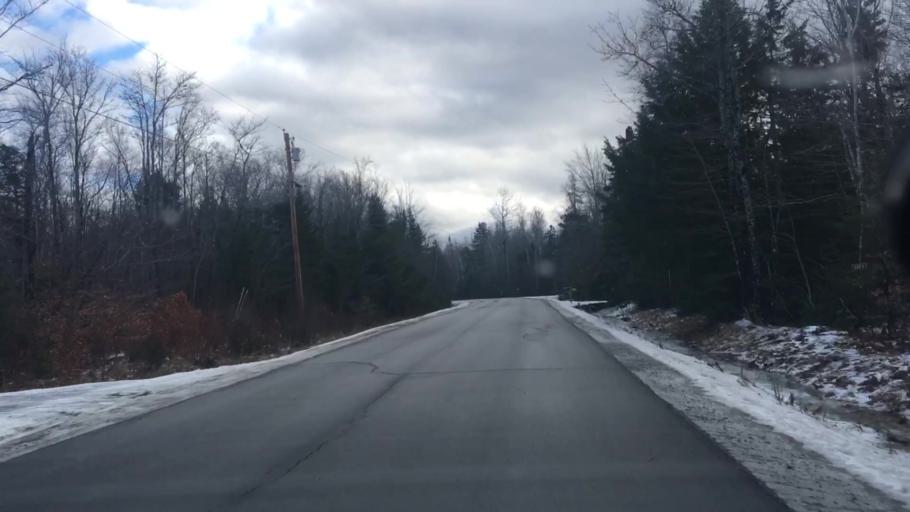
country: US
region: Maine
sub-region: Hancock County
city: Dedham
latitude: 44.6806
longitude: -68.7066
